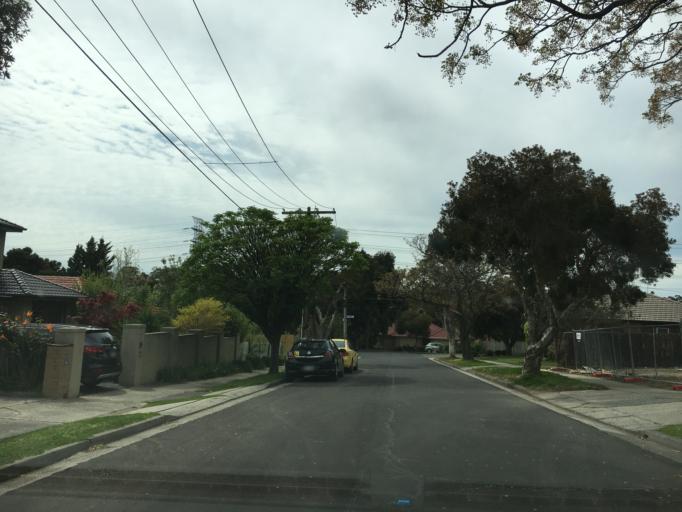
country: AU
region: Victoria
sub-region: Monash
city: Chadstone
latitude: -37.8871
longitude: 145.1015
